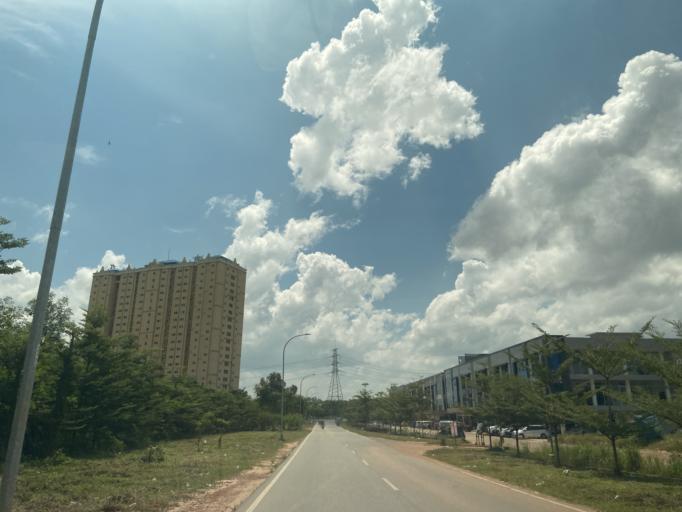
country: SG
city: Singapore
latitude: 1.1160
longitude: 104.0280
